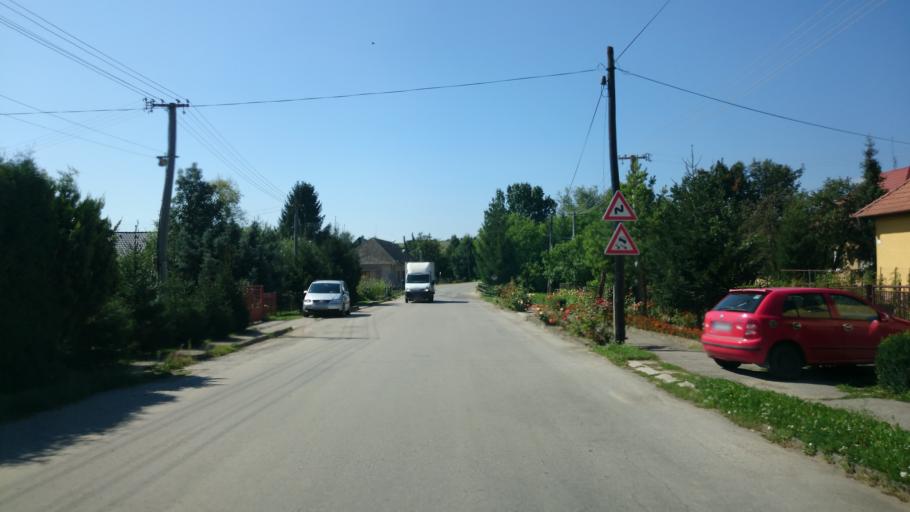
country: SK
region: Nitriansky
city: Banovce nad Bebravou
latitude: 48.7438
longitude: 18.1894
